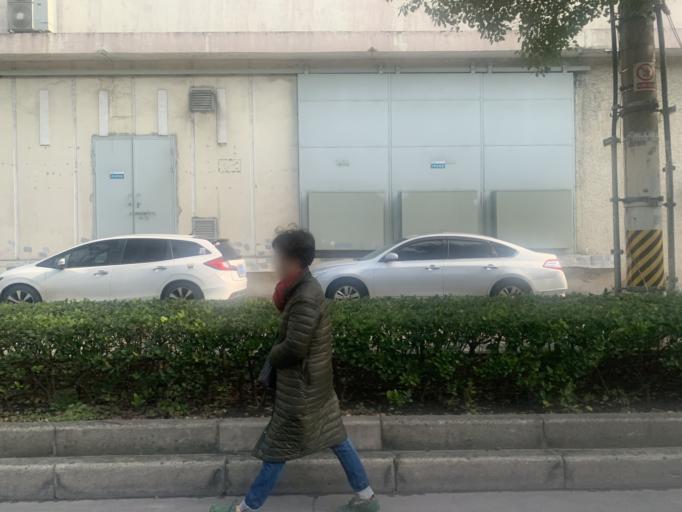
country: CN
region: Shanghai Shi
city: Huamu
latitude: 31.1868
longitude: 121.5141
